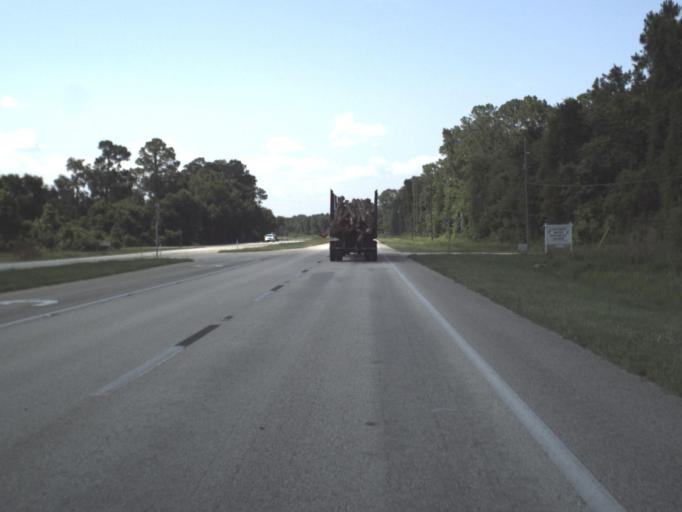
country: US
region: Florida
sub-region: Marion County
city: Citra
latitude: 29.5014
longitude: -82.0990
